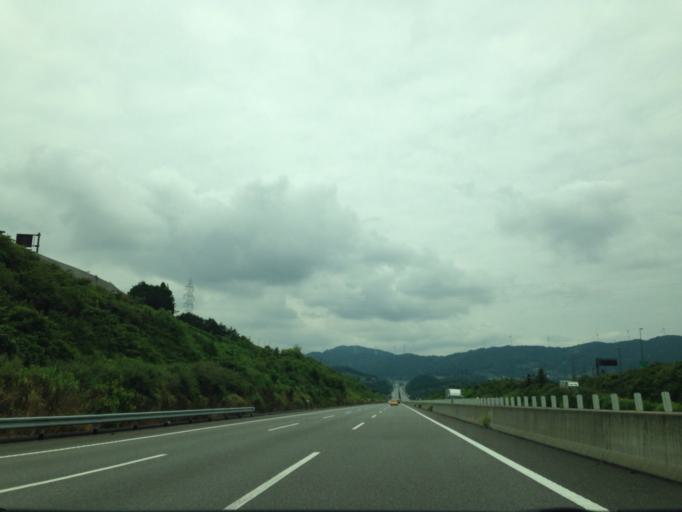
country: JP
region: Shizuoka
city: Hamakita
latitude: 34.8405
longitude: 137.7556
